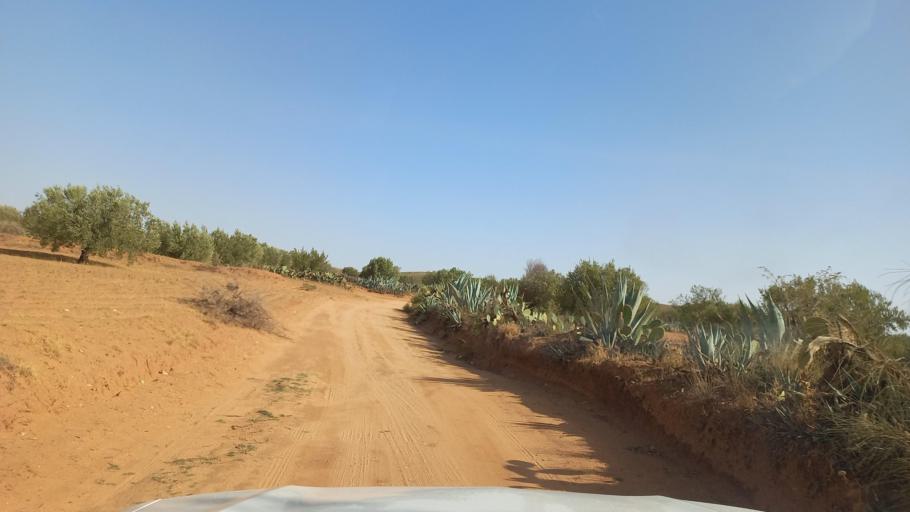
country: TN
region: Al Qasrayn
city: Kasserine
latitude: 35.2027
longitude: 8.9632
